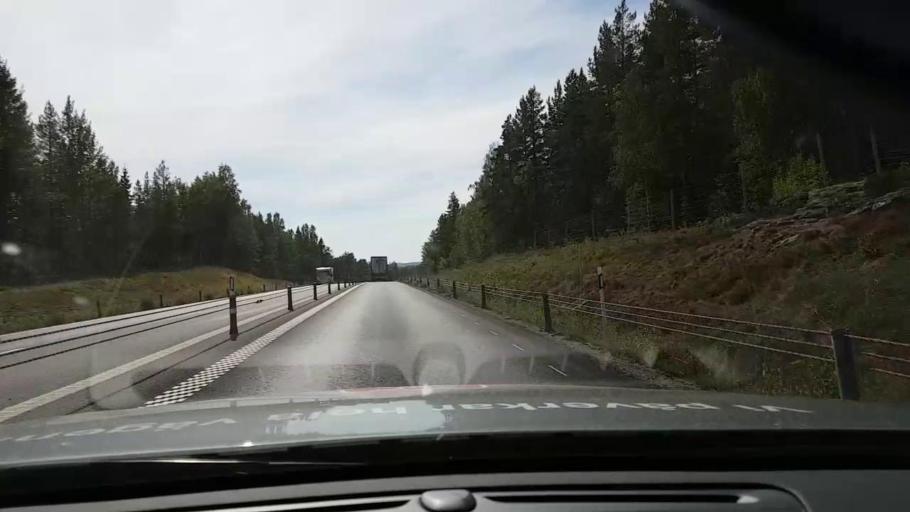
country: SE
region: Vaesternorrland
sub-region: OErnskoeldsviks Kommun
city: Husum
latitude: 63.4762
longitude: 19.2895
